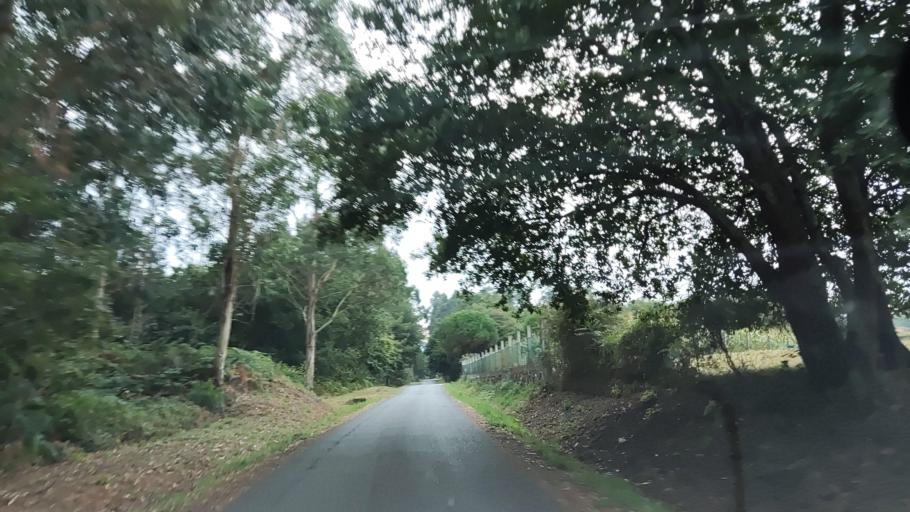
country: ES
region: Galicia
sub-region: Provincia da Coruna
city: Padron
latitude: 42.7157
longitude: -8.6860
